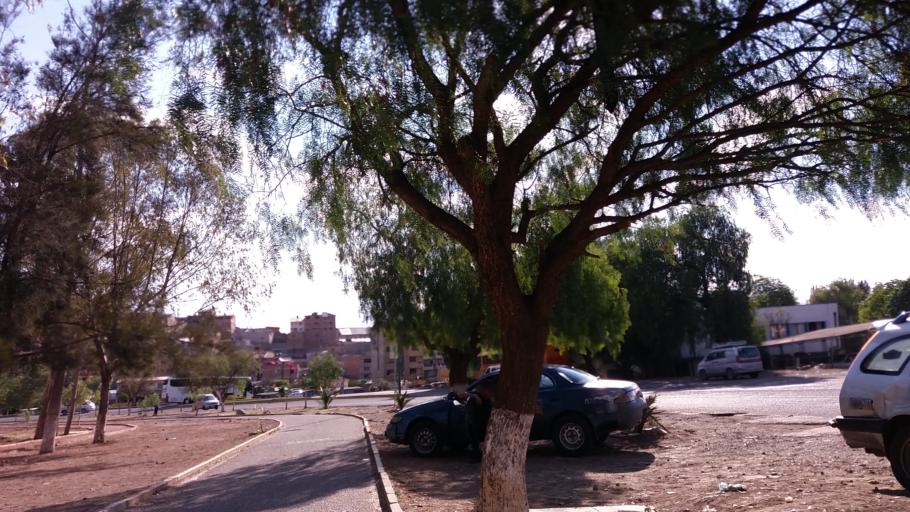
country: BO
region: Cochabamba
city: Cochabamba
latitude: -17.4014
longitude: -66.1461
